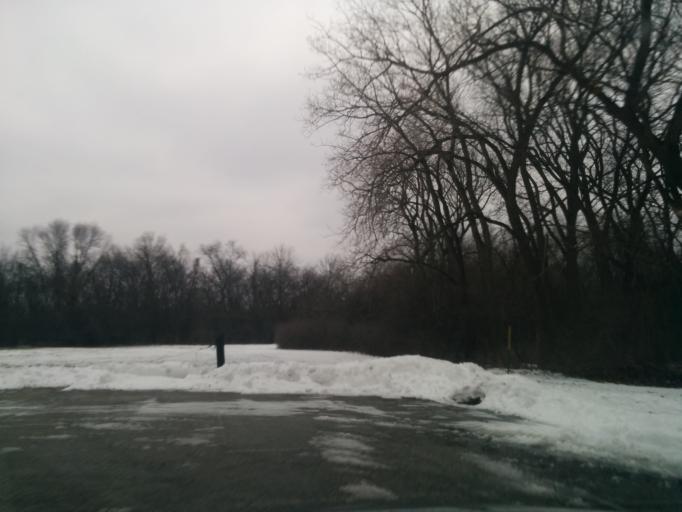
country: US
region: Illinois
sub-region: Cook County
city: Westchester
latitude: 41.8472
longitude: -87.8695
